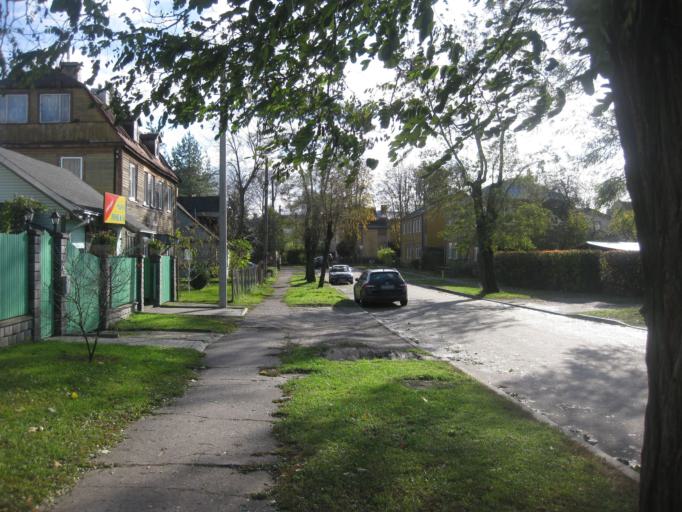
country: LT
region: Kauno apskritis
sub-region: Kaunas
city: Eiguliai
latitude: 54.9063
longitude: 23.9374
